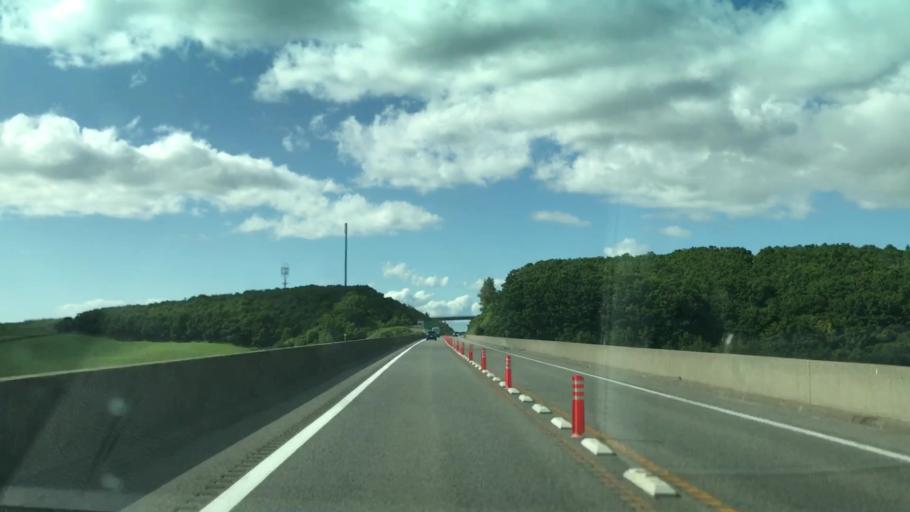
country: JP
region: Hokkaido
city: Muroran
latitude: 42.3933
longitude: 140.9569
